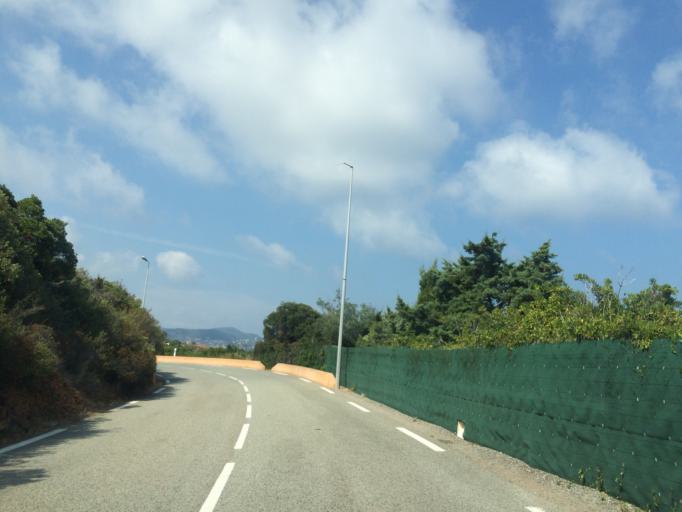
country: FR
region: Provence-Alpes-Cote d'Azur
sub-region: Departement des Alpes-Maritimes
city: Theoule-sur-Mer
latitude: 43.4515
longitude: 6.9198
